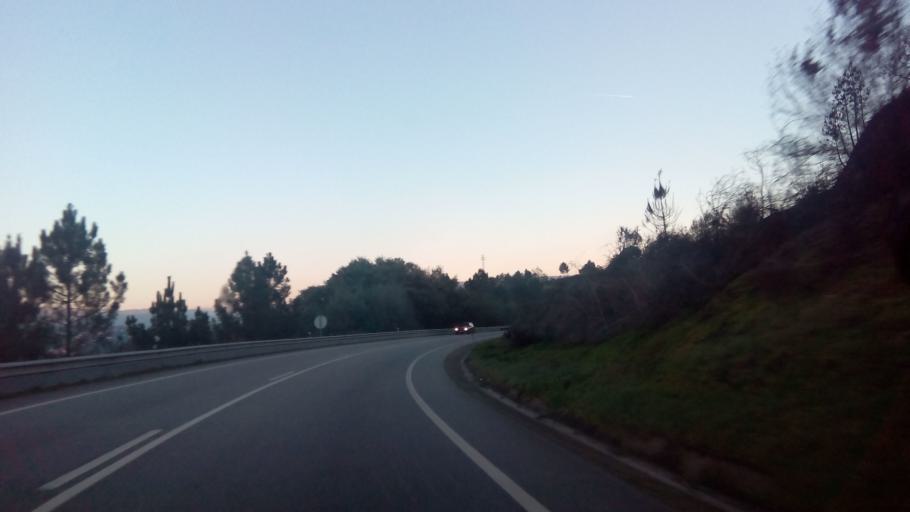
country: PT
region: Porto
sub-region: Amarante
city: Amarante
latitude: 41.2830
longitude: -8.1005
